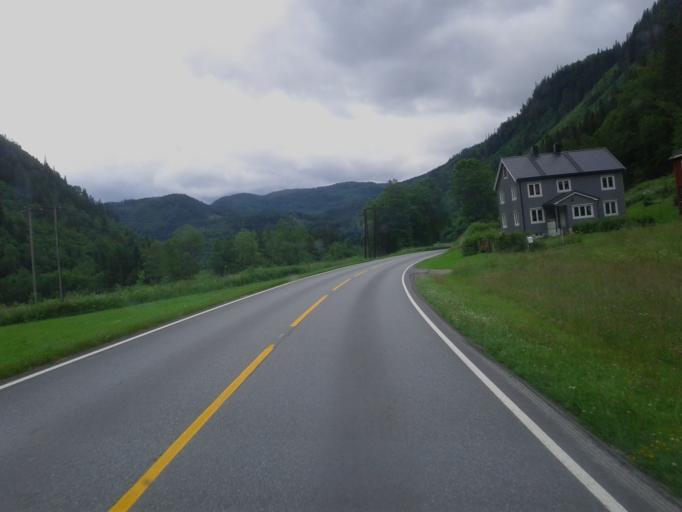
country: NO
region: Sor-Trondelag
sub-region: Midtre Gauldal
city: Storen
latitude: 62.9628
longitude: 10.5852
